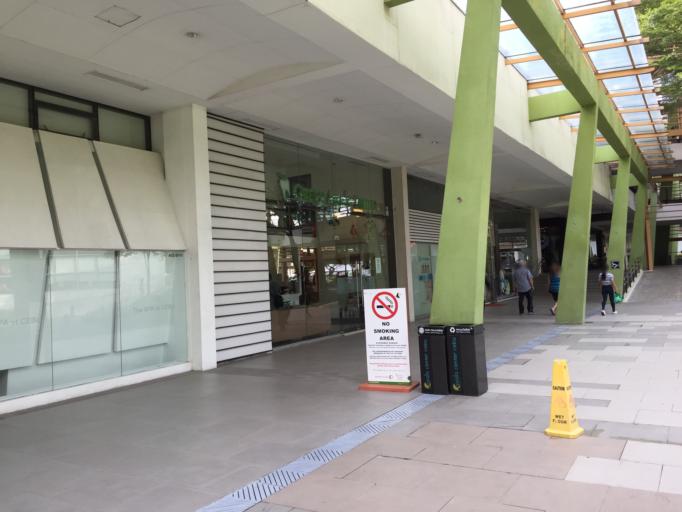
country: PH
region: Central Visayas
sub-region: Cebu City
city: Baugo
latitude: 10.3179
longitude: 123.9063
